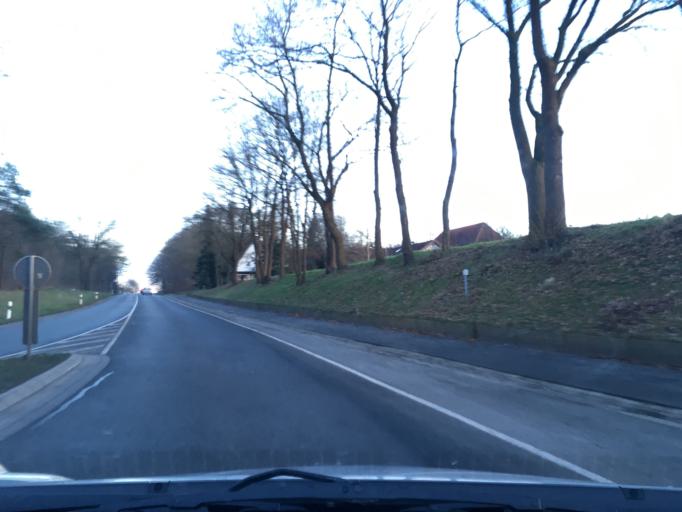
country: DE
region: Lower Saxony
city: Uelzen
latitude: 52.9729
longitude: 10.6008
